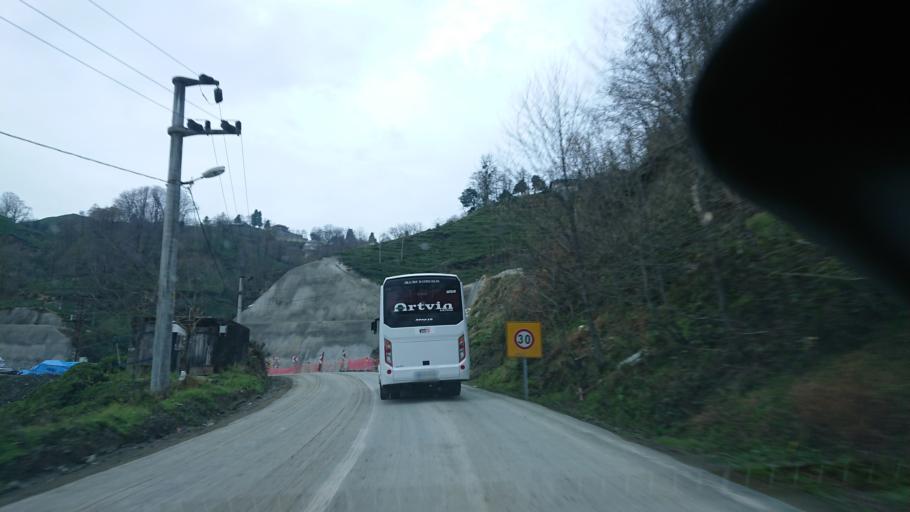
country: TR
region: Rize
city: Rize
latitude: 41.0174
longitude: 40.4978
